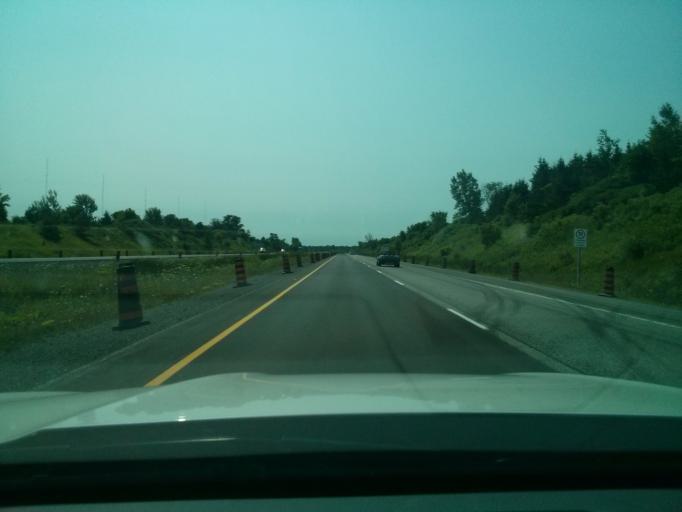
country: CA
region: Ontario
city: Bells Corners
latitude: 45.2614
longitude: -75.7889
